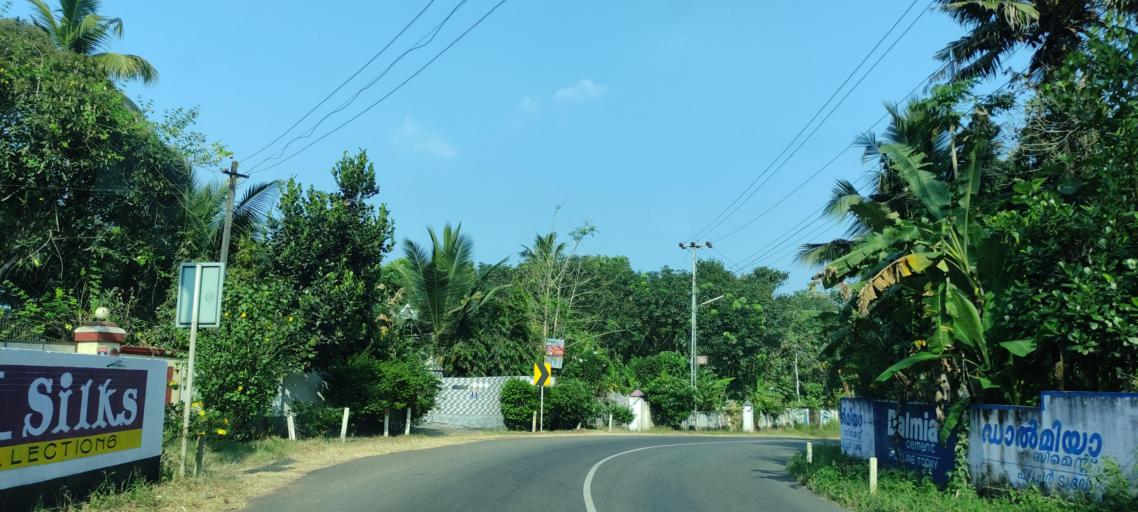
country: IN
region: Kerala
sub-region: Pattanamtitta
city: Adur
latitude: 9.0717
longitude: 76.6538
